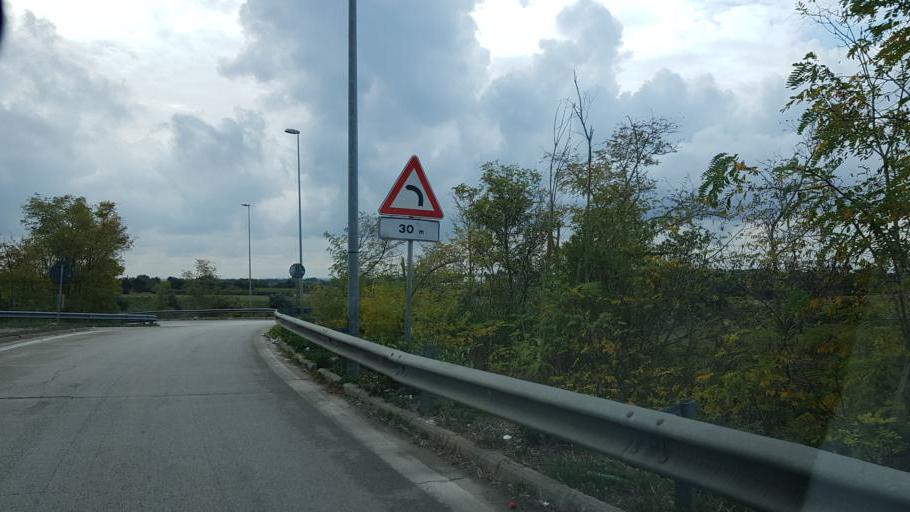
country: IT
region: Apulia
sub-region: Provincia di Bari
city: Triggiano
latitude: 41.0866
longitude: 16.8940
